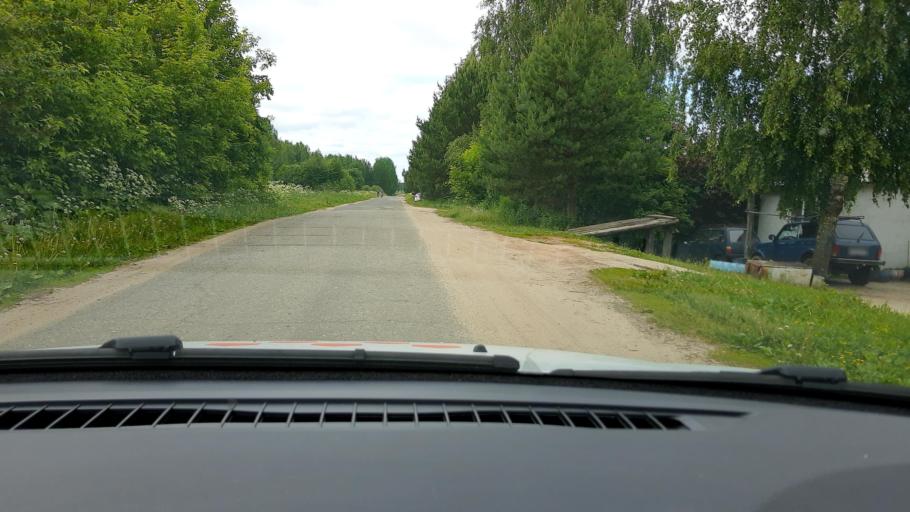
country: RU
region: Nizjnij Novgorod
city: Sitniki
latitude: 56.5219
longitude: 44.1097
